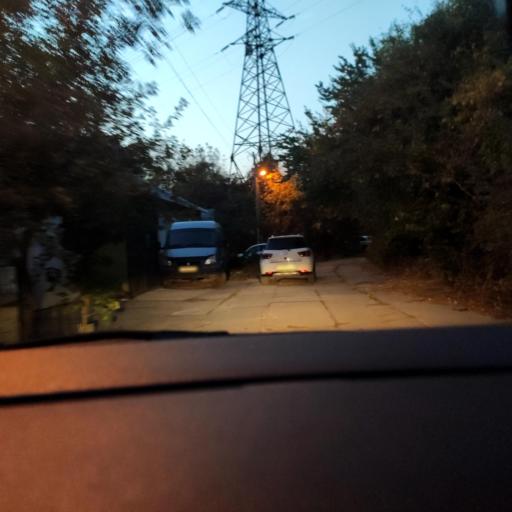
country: RU
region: Voronezj
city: Voronezh
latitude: 51.6822
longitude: 39.1585
